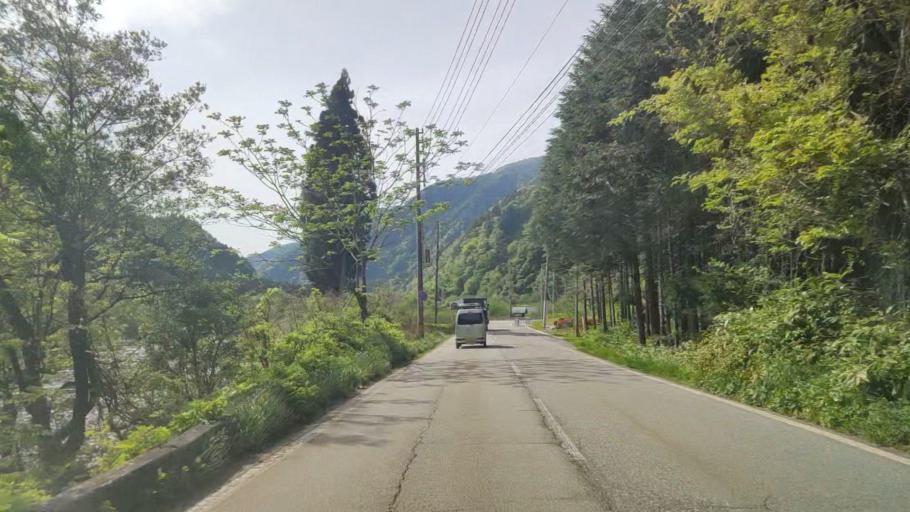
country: JP
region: Gifu
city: Takayama
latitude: 36.2520
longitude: 137.4789
